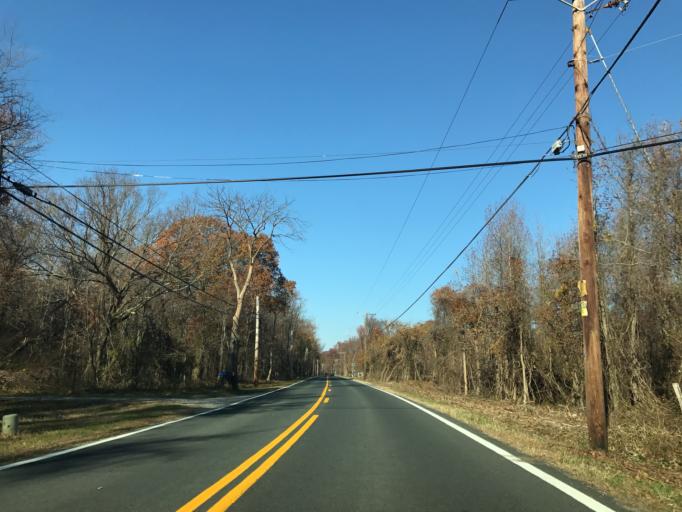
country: US
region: Maryland
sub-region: Anne Arundel County
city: Lake Shore
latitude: 39.1004
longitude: -76.4342
